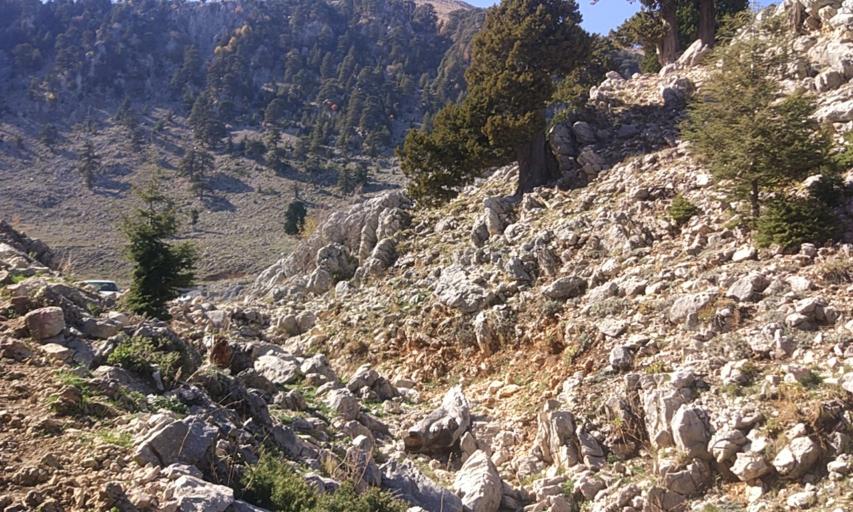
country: TR
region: Antalya
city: Altinyaka
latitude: 36.5497
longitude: 30.4128
